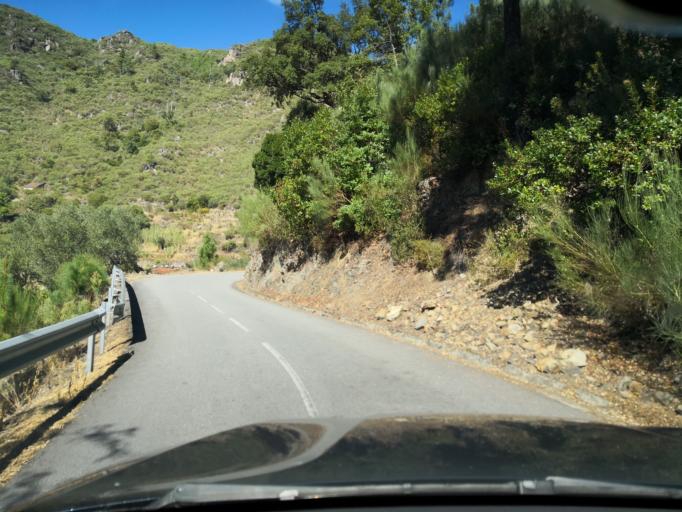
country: PT
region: Vila Real
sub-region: Santa Marta de Penaguiao
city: Santa Marta de Penaguiao
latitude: 41.2589
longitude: -7.7988
